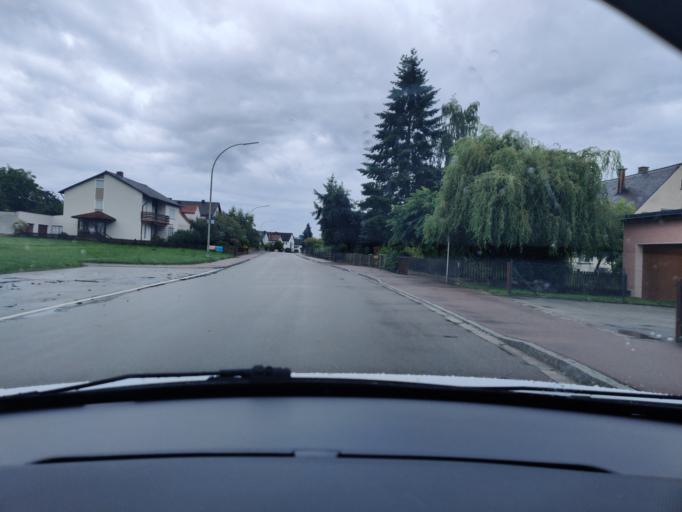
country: DE
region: Bavaria
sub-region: Upper Palatinate
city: Pfreimd
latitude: 49.4989
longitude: 12.1846
